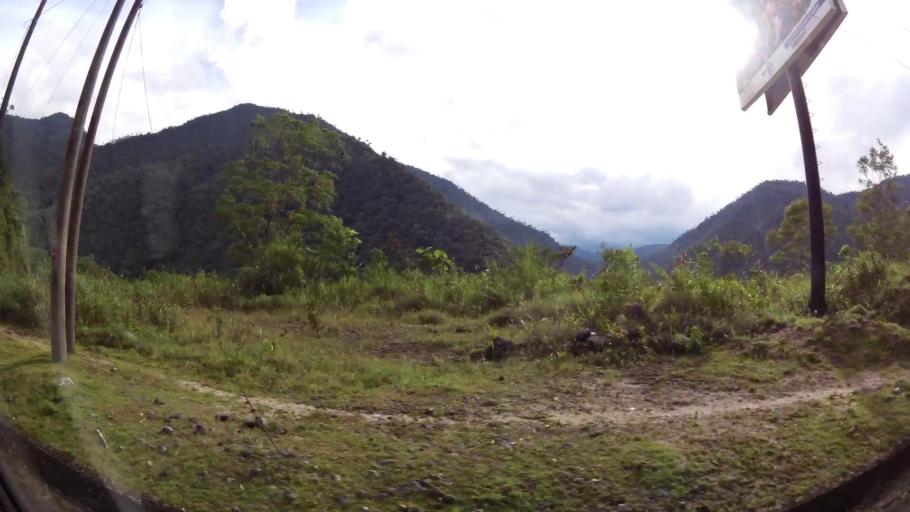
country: EC
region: Pastaza
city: Puyo
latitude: -1.4466
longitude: -78.1751
